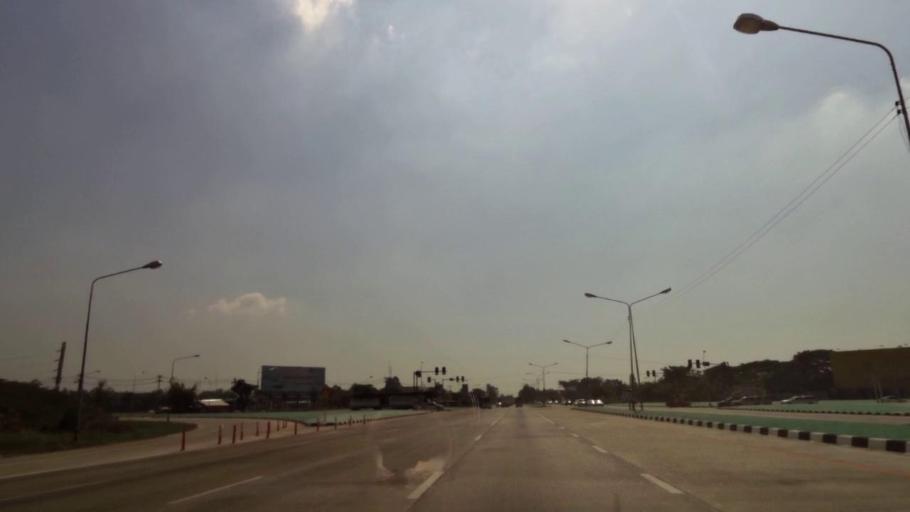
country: TH
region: Phichit
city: Bueng Na Rang
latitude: 16.1245
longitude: 100.1256
